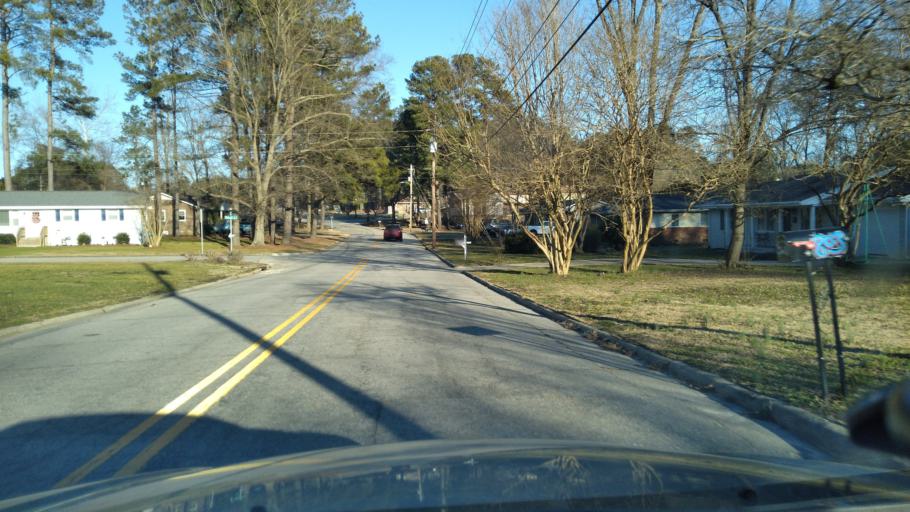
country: US
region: North Carolina
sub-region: Wake County
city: Garner
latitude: 35.6976
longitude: -78.6185
